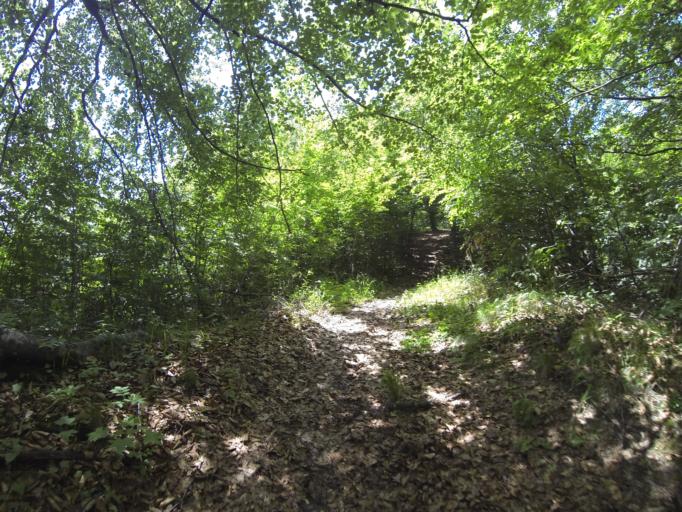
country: RO
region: Valcea
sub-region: Oras Baile Olanesti
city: Baile Olanesti
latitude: 45.2195
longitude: 24.1970
